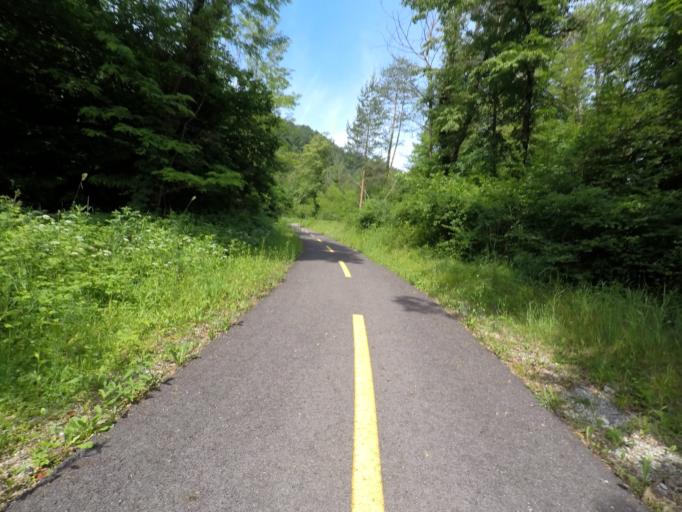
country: IT
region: Friuli Venezia Giulia
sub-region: Provincia di Udine
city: Tolmezzo
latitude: 46.3844
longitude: 13.0144
